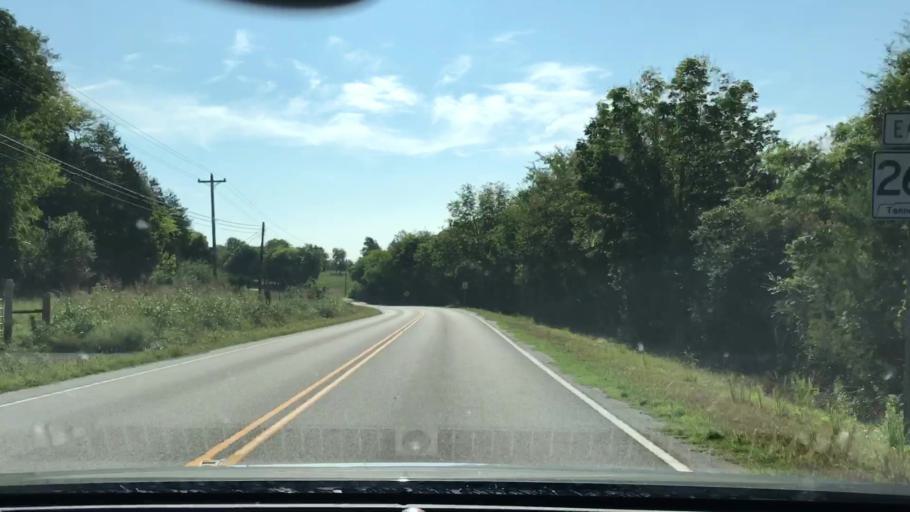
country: US
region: Tennessee
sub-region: Jackson County
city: Gainesboro
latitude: 36.3553
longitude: -85.7197
